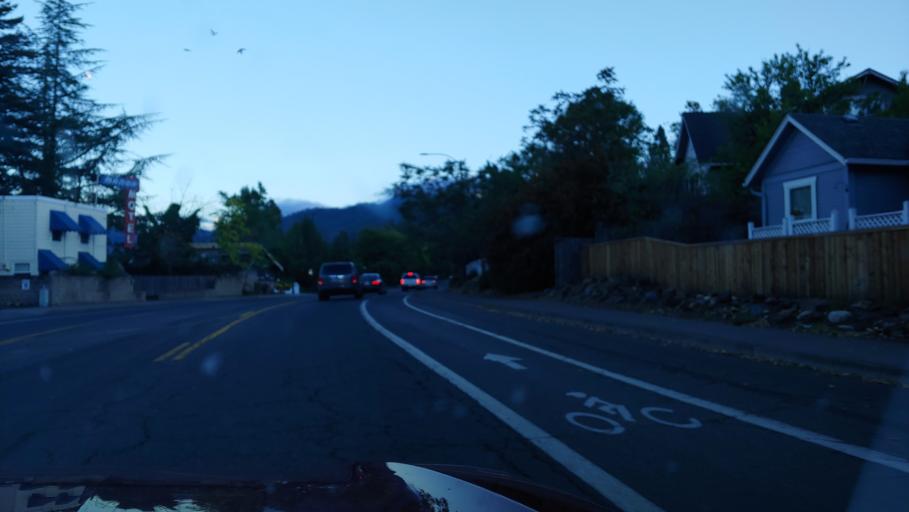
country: US
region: Oregon
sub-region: Jackson County
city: Ashland
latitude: 42.2055
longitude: -122.7205
